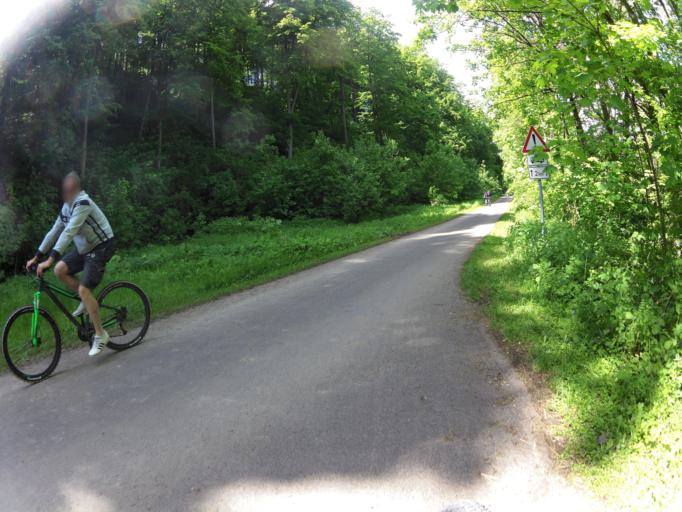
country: DE
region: Thuringia
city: Ebenshausen
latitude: 51.0857
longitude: 10.3060
